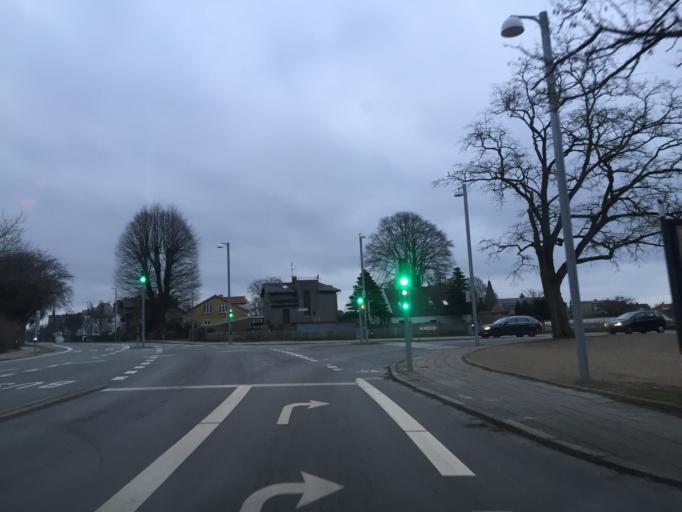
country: DK
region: South Denmark
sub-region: Haderslev Kommune
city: Haderslev
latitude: 55.2536
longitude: 9.4898
